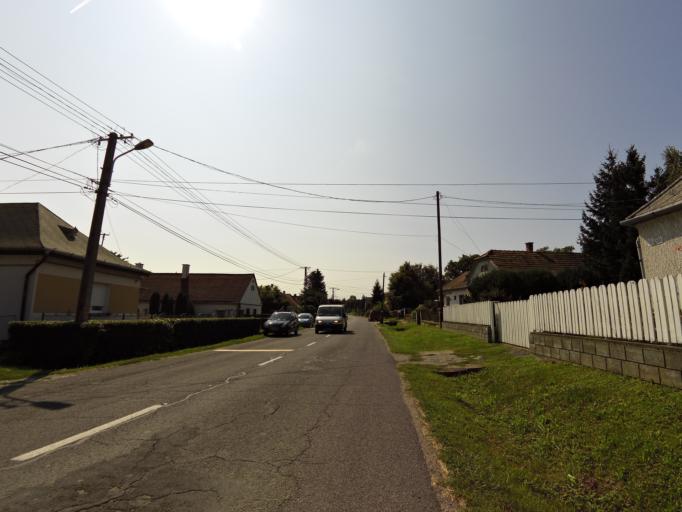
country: HU
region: Zala
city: Vonyarcvashegy
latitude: 46.8062
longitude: 17.3814
